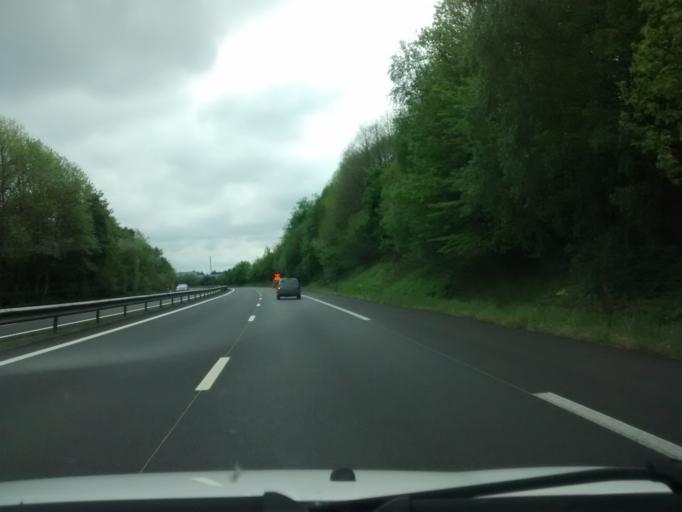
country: FR
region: Brittany
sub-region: Departement des Cotes-d'Armor
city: Plouer-sur-Rance
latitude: 48.5274
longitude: -2.0329
